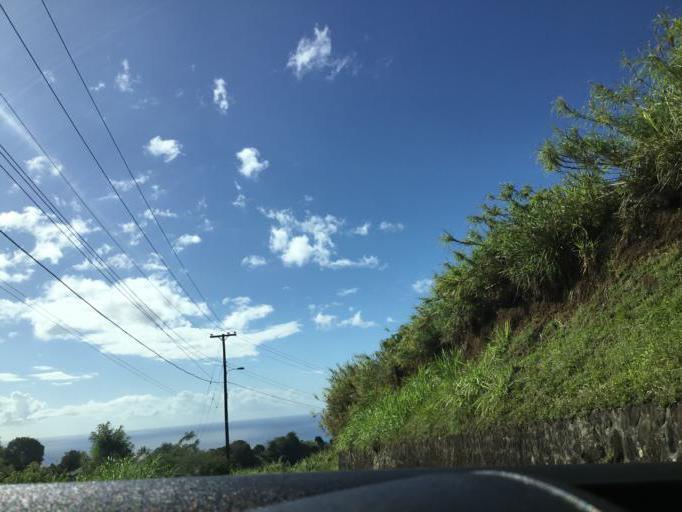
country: VC
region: Saint David
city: Chateaubelair
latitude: 13.2755
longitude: -61.2484
